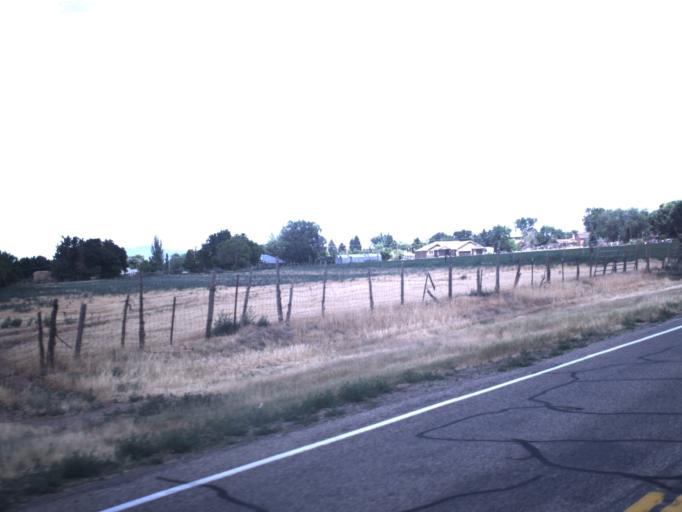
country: US
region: Utah
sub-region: Iron County
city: Parowan
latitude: 37.8793
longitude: -112.7798
